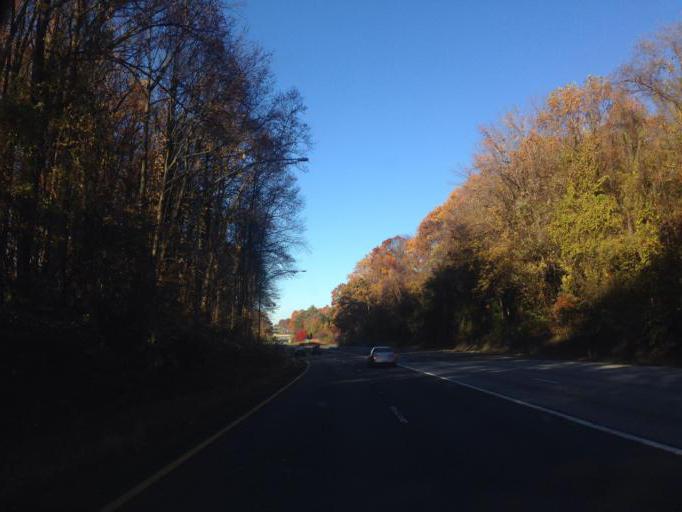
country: US
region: Maryland
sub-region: Howard County
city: Ellicott City
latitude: 39.2967
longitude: -76.8172
